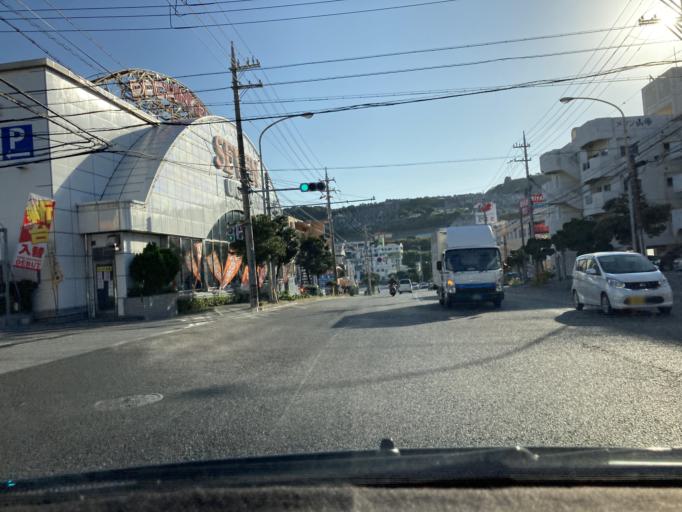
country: JP
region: Okinawa
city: Ginowan
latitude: 26.2490
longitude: 127.7386
